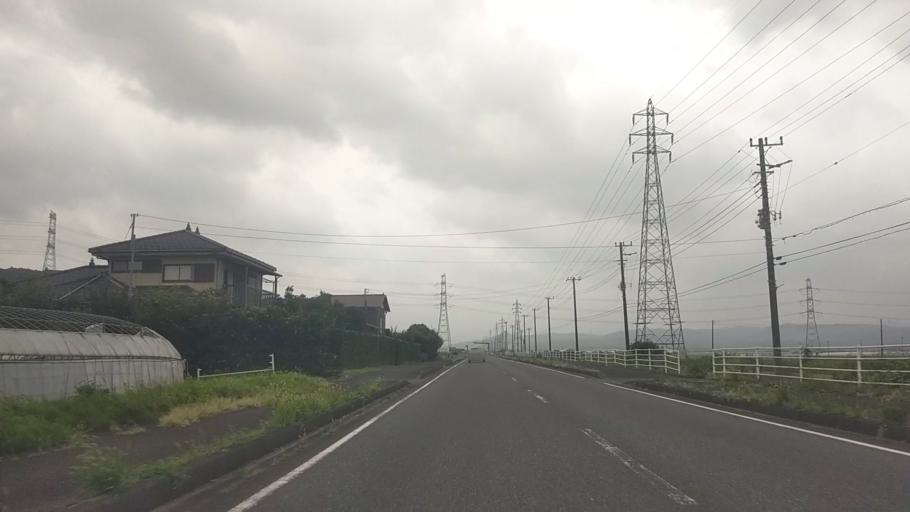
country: JP
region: Chiba
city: Kisarazu
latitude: 35.3484
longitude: 140.0548
